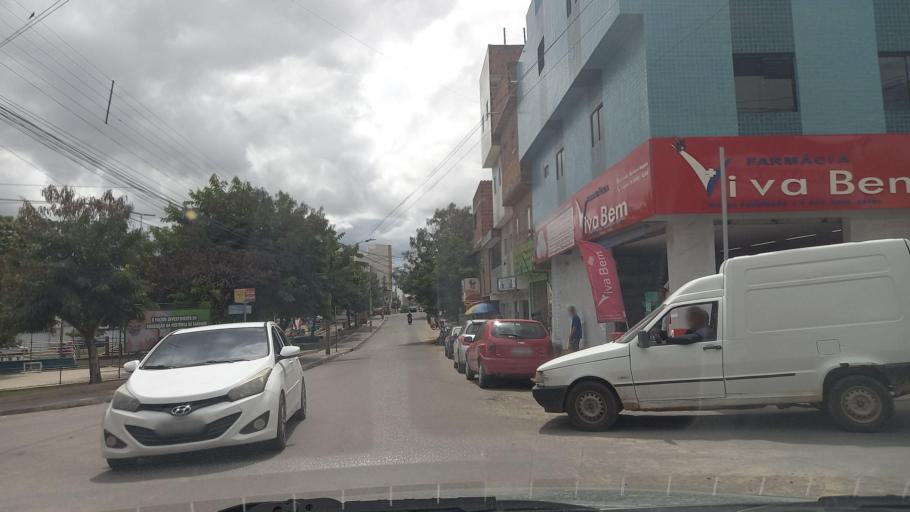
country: BR
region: Pernambuco
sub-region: Caruaru
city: Caruaru
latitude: -8.2728
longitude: -35.9597
